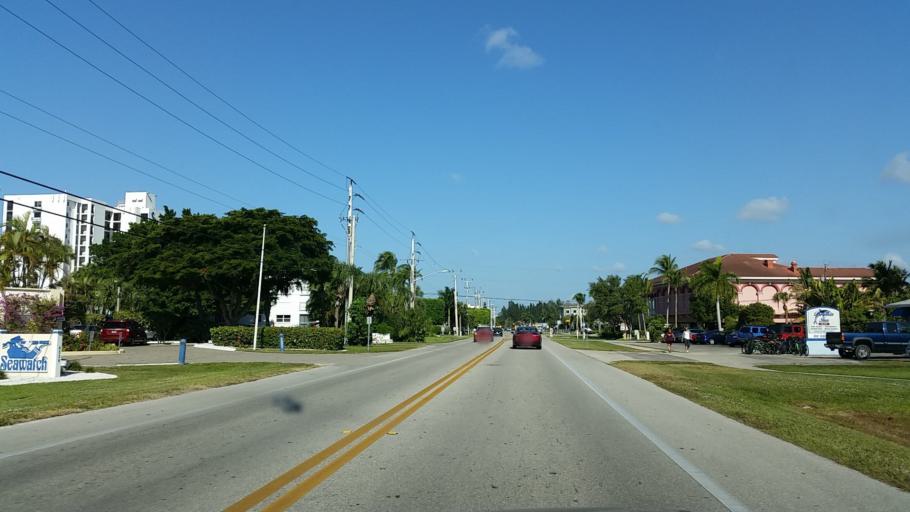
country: US
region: Florida
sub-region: Lee County
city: Fort Myers Beach
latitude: 26.4207
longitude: -81.9032
